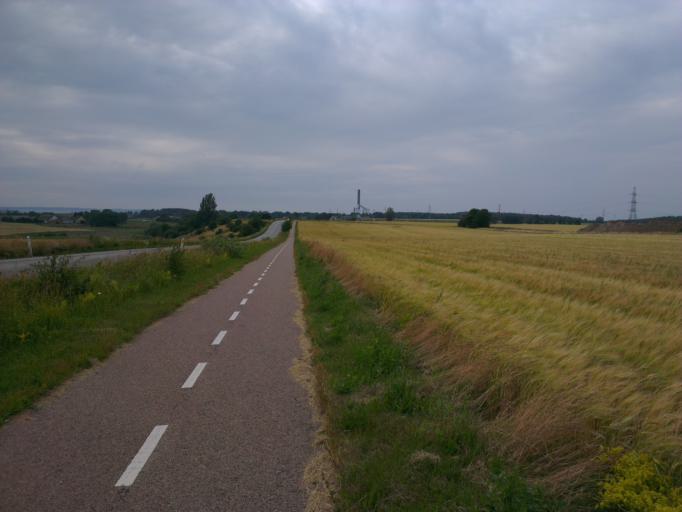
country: DK
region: Capital Region
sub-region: Frederikssund Kommune
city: Skibby
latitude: 55.7999
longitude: 11.9040
